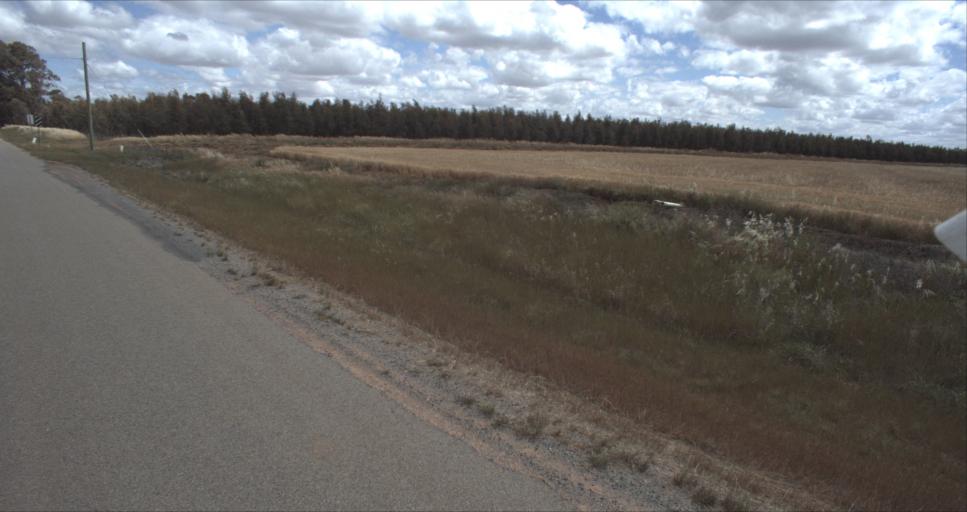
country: AU
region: New South Wales
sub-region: Leeton
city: Leeton
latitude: -34.5734
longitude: 146.3987
